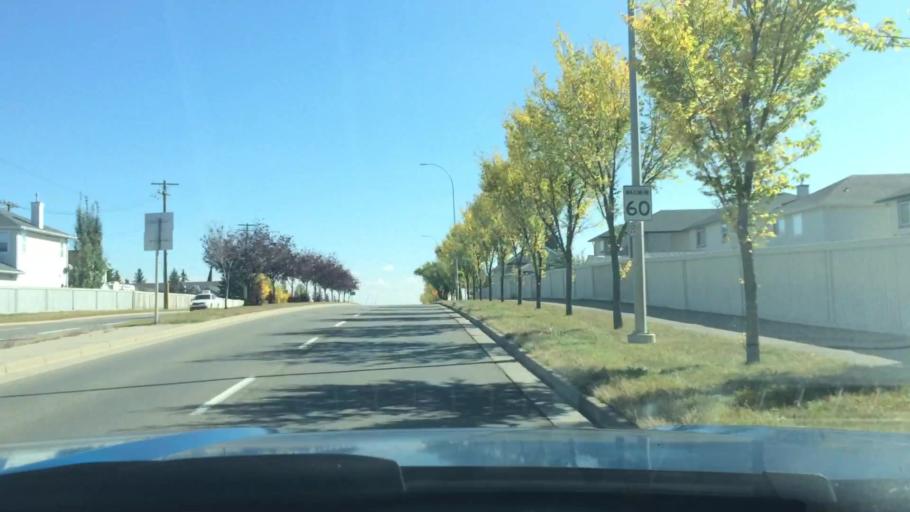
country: CA
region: Alberta
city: Calgary
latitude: 50.9140
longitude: -114.0959
